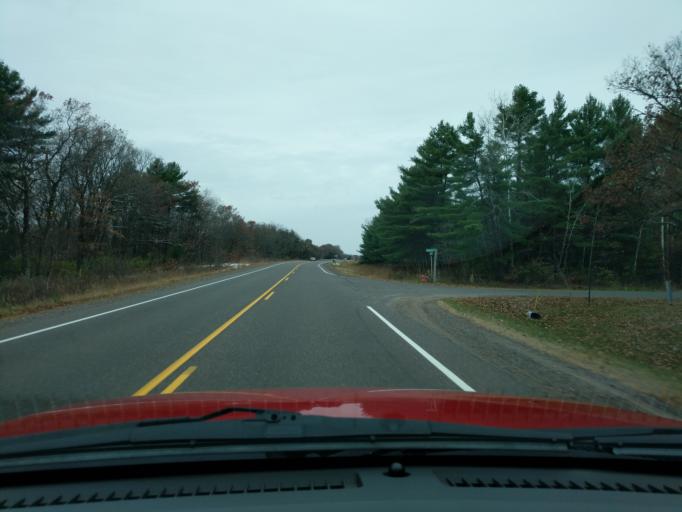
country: US
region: Wisconsin
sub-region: Burnett County
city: Siren
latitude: 45.8244
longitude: -92.2567
